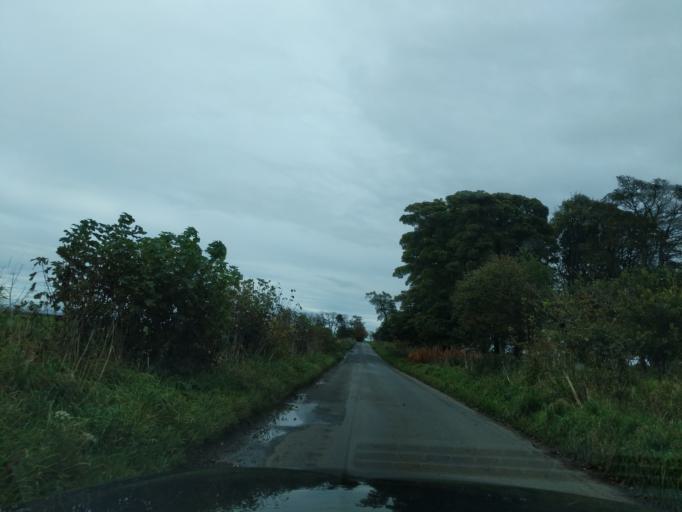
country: GB
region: Scotland
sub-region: Fife
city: Saint Andrews
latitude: 56.2893
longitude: -2.7934
